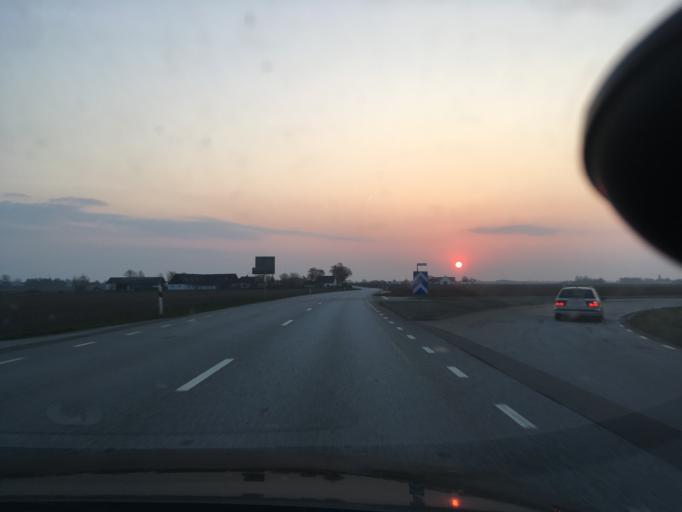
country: SE
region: Skane
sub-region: Ystads Kommun
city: Kopingebro
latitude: 55.4403
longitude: 13.9932
